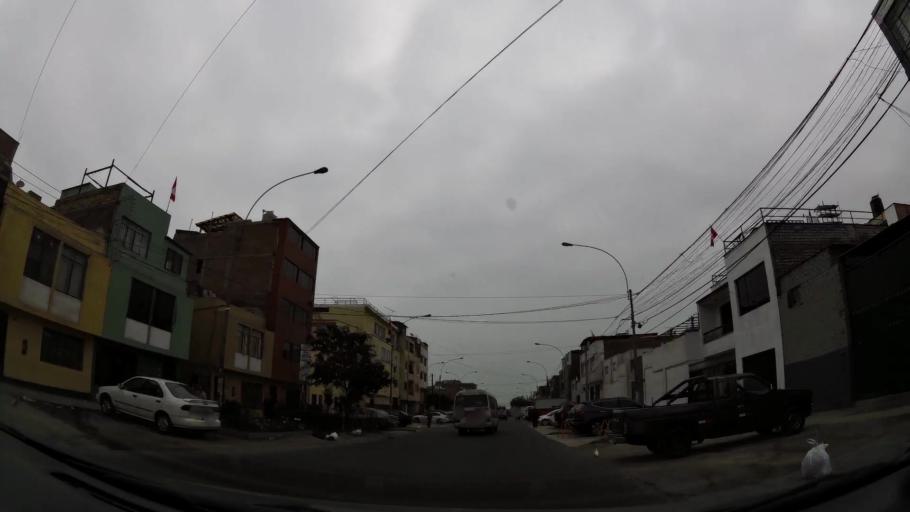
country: PE
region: Lima
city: Lima
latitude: -12.0551
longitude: -77.0587
